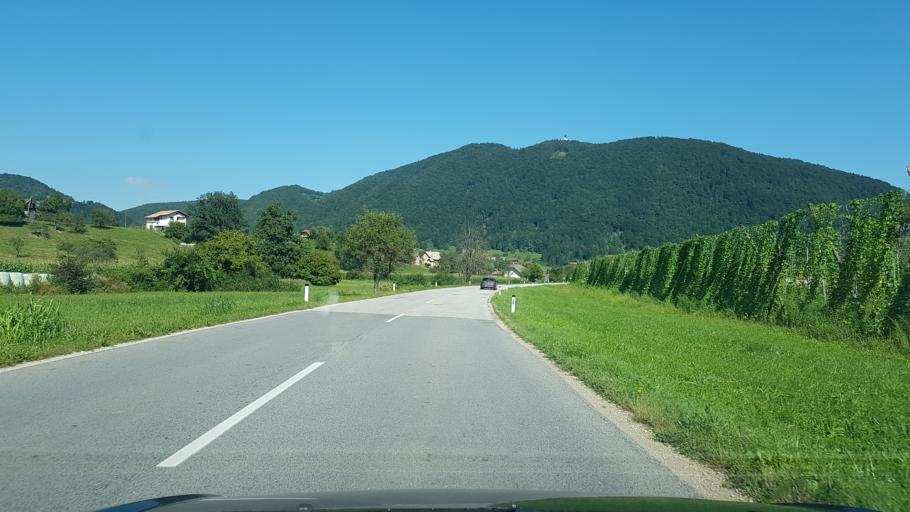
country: SI
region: Smartno ob Paki
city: Smartno ob Paki
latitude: 46.3199
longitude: 15.0313
